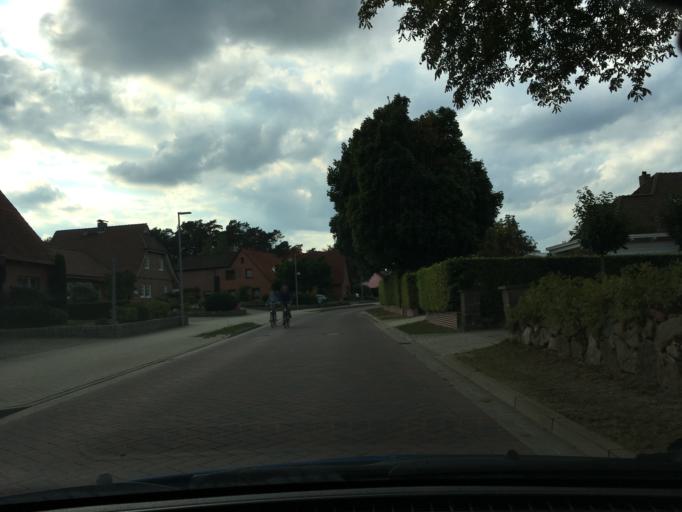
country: DE
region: Lower Saxony
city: Garstedt
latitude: 53.2875
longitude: 10.1561
